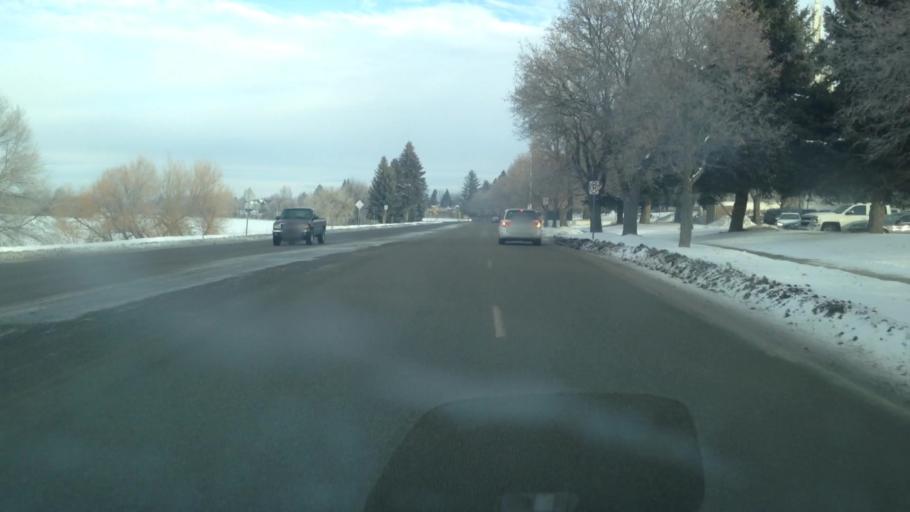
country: US
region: Idaho
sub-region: Bonneville County
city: Idaho Falls
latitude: 43.4980
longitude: -112.0418
